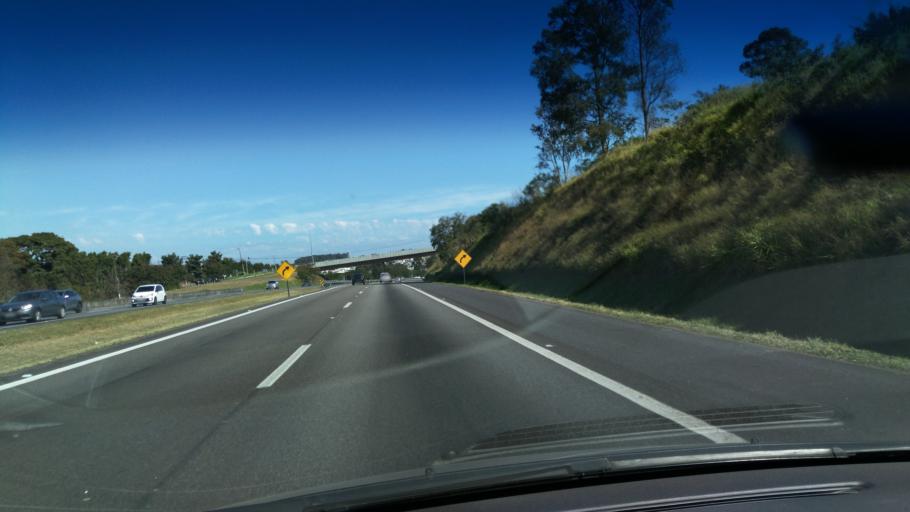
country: BR
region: Sao Paulo
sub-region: Valinhos
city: Valinhos
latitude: -22.9485
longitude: -47.0164
